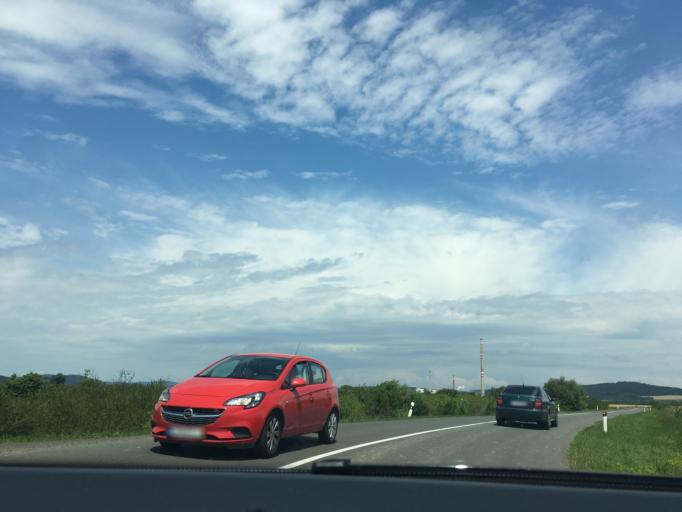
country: SK
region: Presovsky
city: Vranov nad Topl'ou
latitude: 48.8455
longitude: 21.7163
